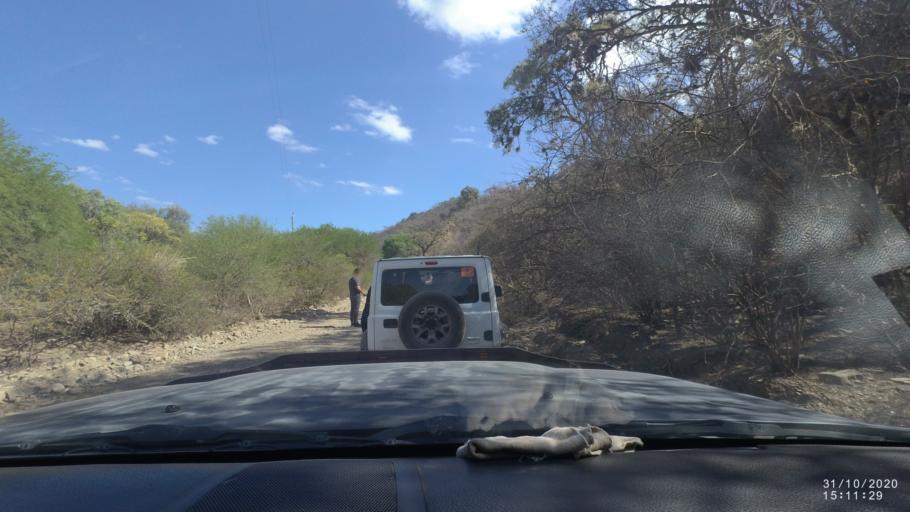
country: BO
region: Cochabamba
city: Aiquile
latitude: -18.3209
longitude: -64.7806
